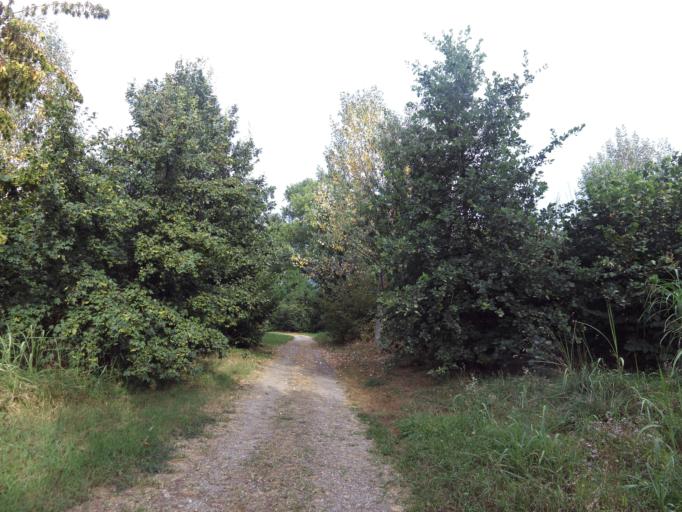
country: IT
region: Lombardy
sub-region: Citta metropolitana di Milano
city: San Giuliano Milanese
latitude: 45.3862
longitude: 9.2952
